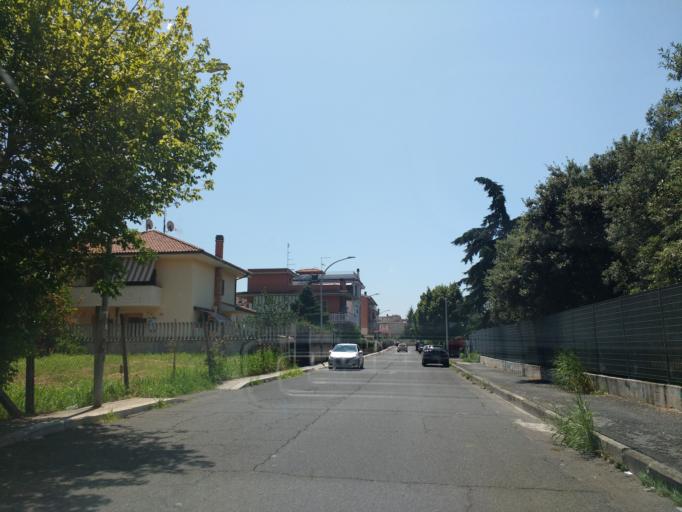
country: IT
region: Latium
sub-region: Citta metropolitana di Roma Capitale
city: Villa Adriana
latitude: 41.9532
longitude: 12.7716
